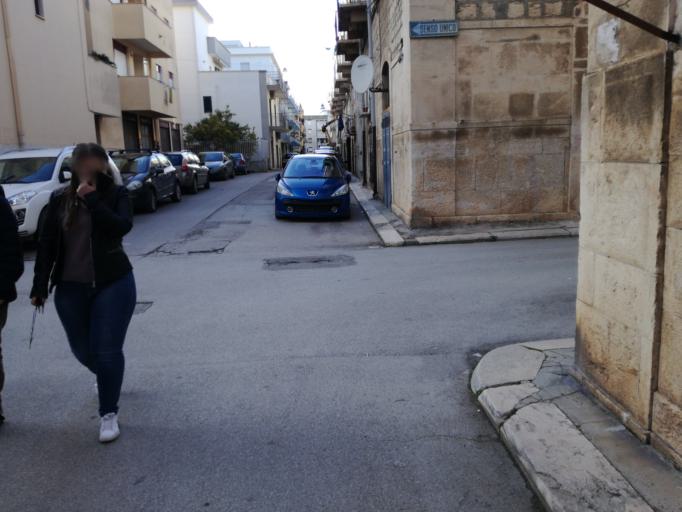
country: IT
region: Apulia
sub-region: Provincia di Bari
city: Ruvo di Puglia
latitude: 41.1163
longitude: 16.4812
